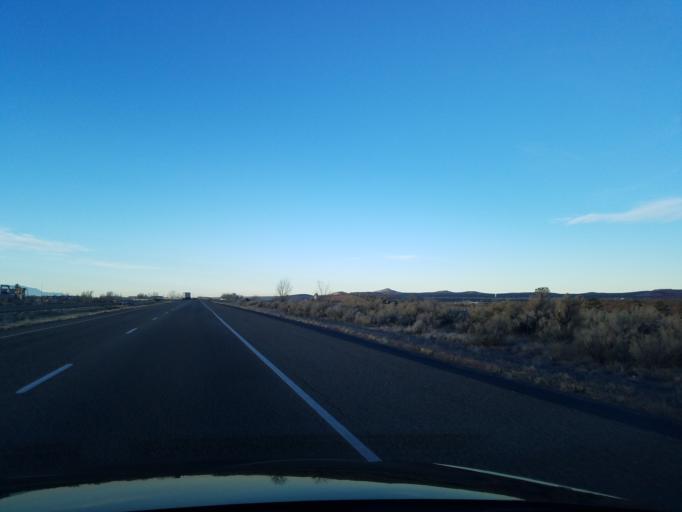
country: US
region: New Mexico
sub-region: Santa Fe County
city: Agua Fria
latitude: 35.6405
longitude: -106.0667
